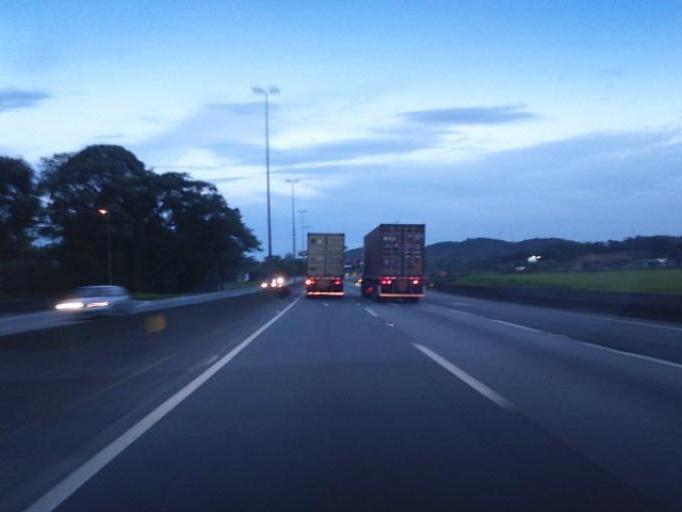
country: BR
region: Santa Catarina
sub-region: Joinville
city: Joinville
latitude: -26.3863
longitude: -48.8449
